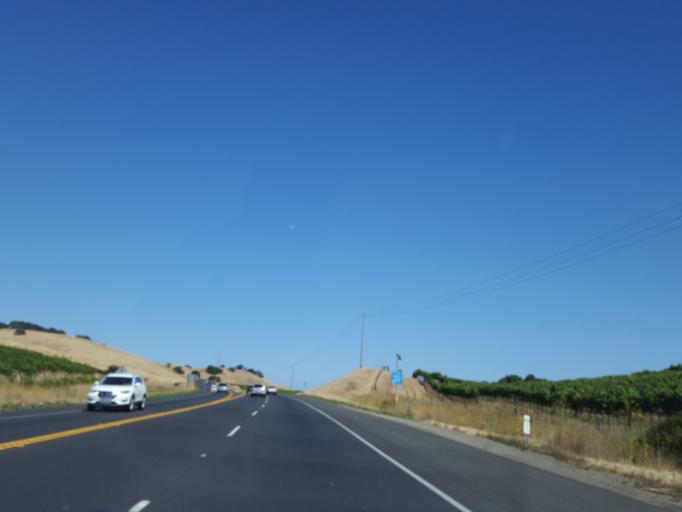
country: US
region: California
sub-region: Sonoma County
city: Sonoma
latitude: 38.2529
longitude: -122.3909
